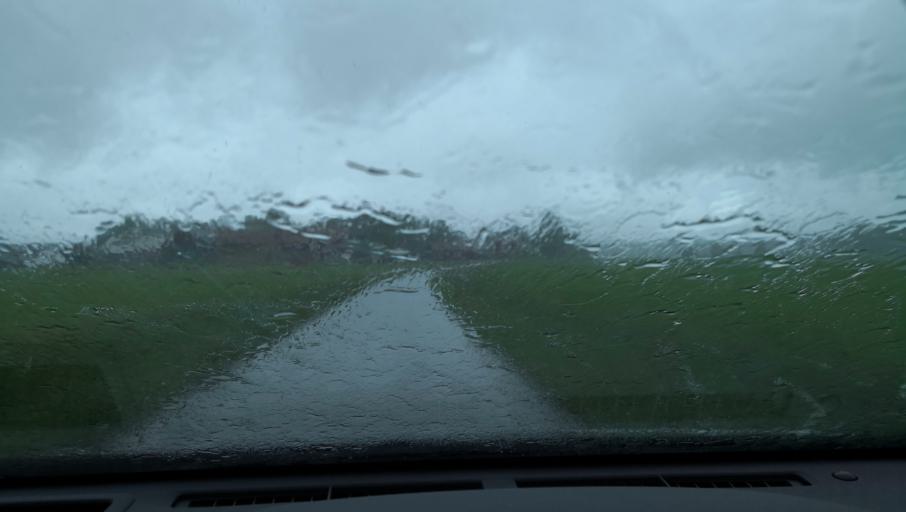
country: SE
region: Uppsala
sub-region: Enkopings Kommun
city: Orsundsbro
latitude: 59.7775
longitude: 17.3496
